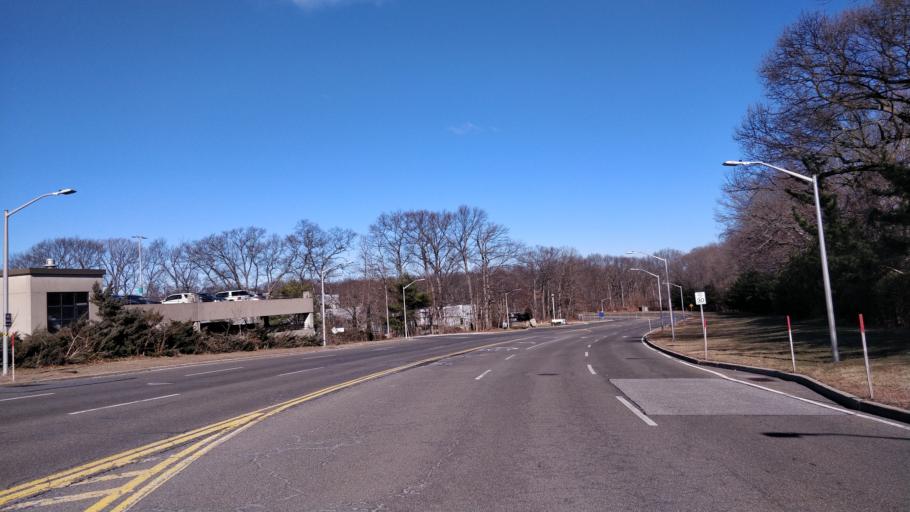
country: US
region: New York
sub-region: Suffolk County
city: Setauket-East Setauket
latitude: 40.9109
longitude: -73.1132
